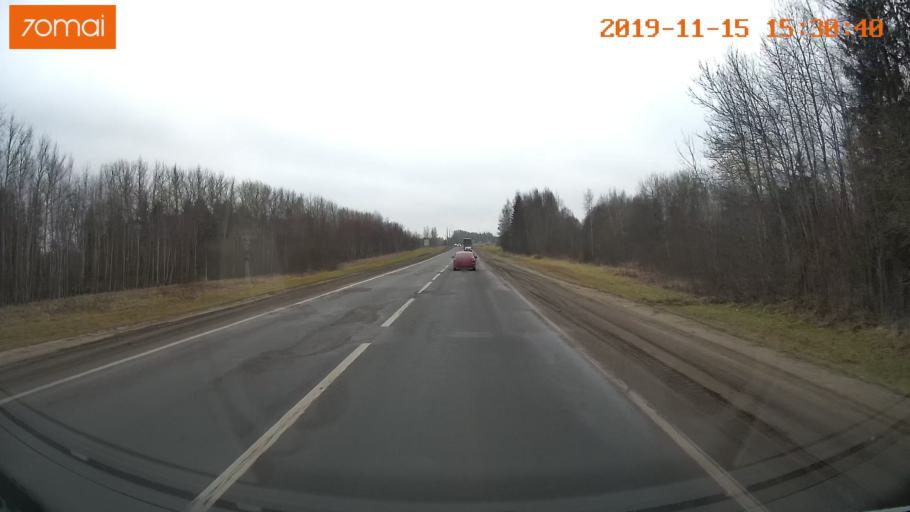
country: RU
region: Jaroslavl
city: Danilov
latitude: 58.1078
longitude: 40.1119
